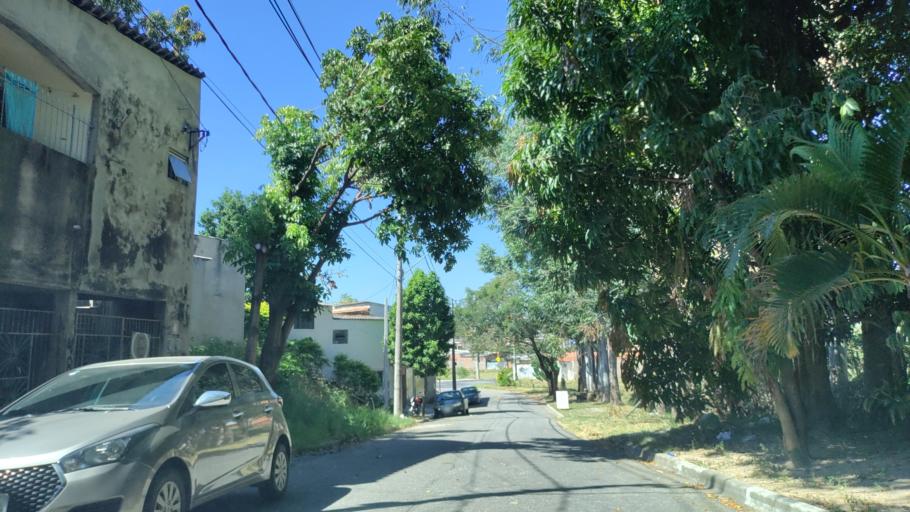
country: BR
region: Sao Paulo
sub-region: Sorocaba
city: Sorocaba
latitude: -23.4681
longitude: -47.4670
